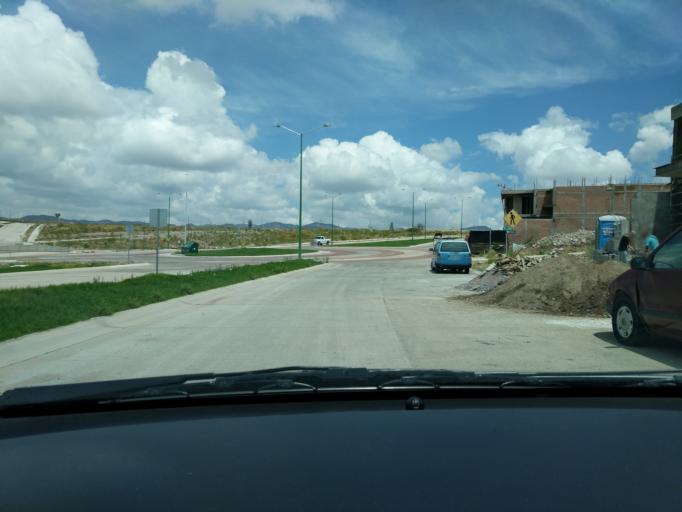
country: MX
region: San Luis Potosi
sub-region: Mexquitic de Carmona
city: Guadalupe Victoria
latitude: 22.1550
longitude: -101.0511
